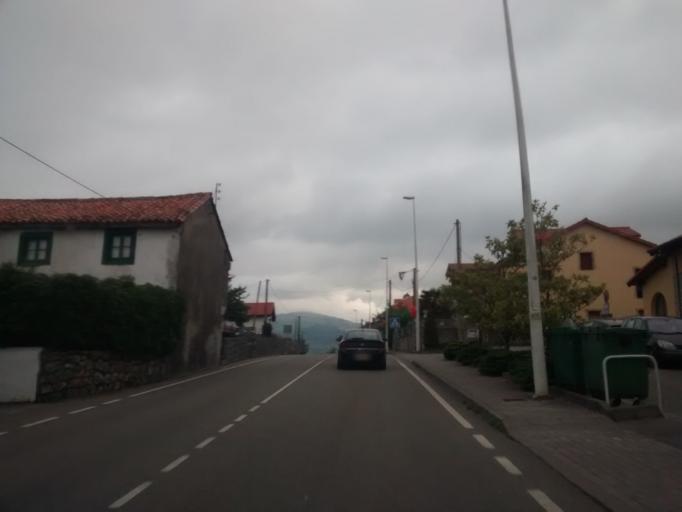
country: ES
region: Cantabria
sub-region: Provincia de Cantabria
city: Santander
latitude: 43.4404
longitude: -3.7691
